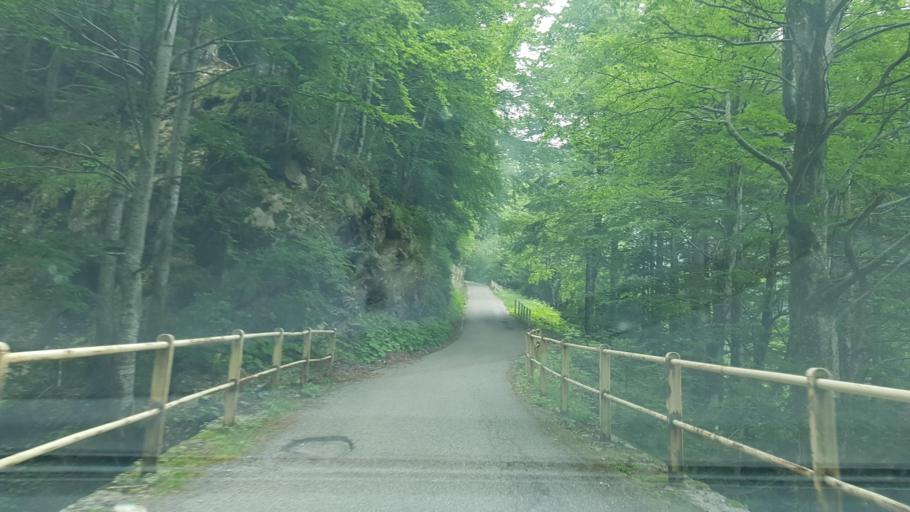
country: IT
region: Friuli Venezia Giulia
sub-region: Provincia di Udine
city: Paularo
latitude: 46.5801
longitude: 13.1315
